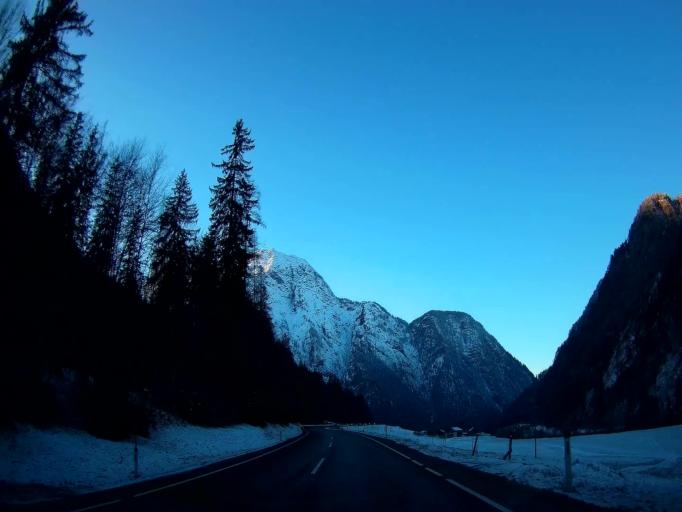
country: AT
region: Salzburg
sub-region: Politischer Bezirk Zell am See
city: Sankt Martin bei Lofer
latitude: 47.5291
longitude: 12.7356
